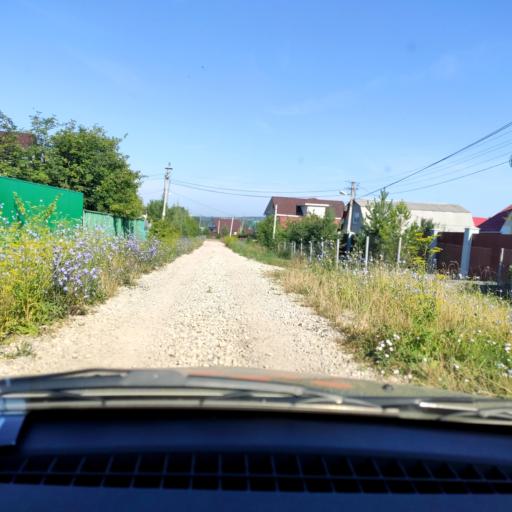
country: RU
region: Bashkortostan
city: Avdon
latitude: 54.5933
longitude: 55.6979
